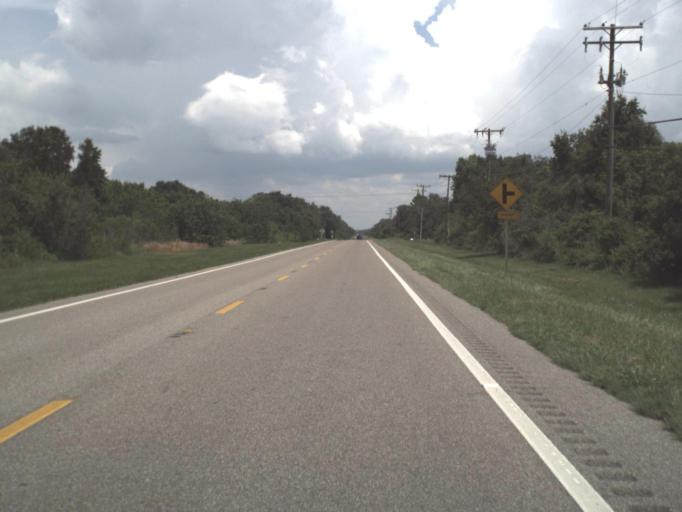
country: US
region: Florida
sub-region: Hillsborough County
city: Sun City Center
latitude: 27.6886
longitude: -82.3435
